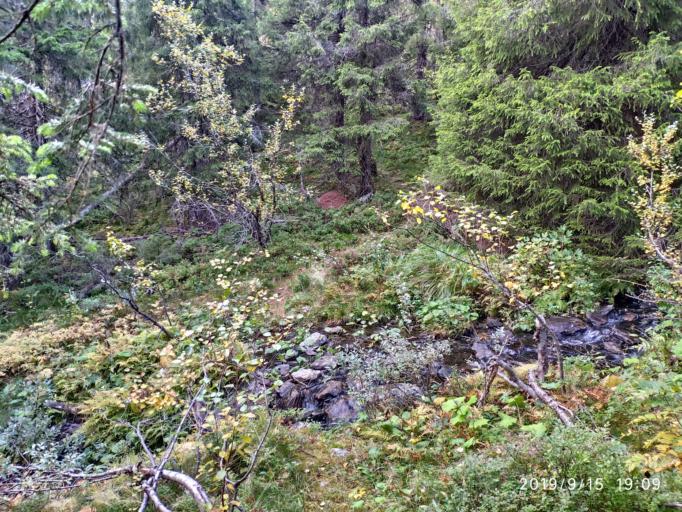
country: NO
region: Oppland
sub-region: Oyer
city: Tretten
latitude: 61.4146
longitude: 10.2625
